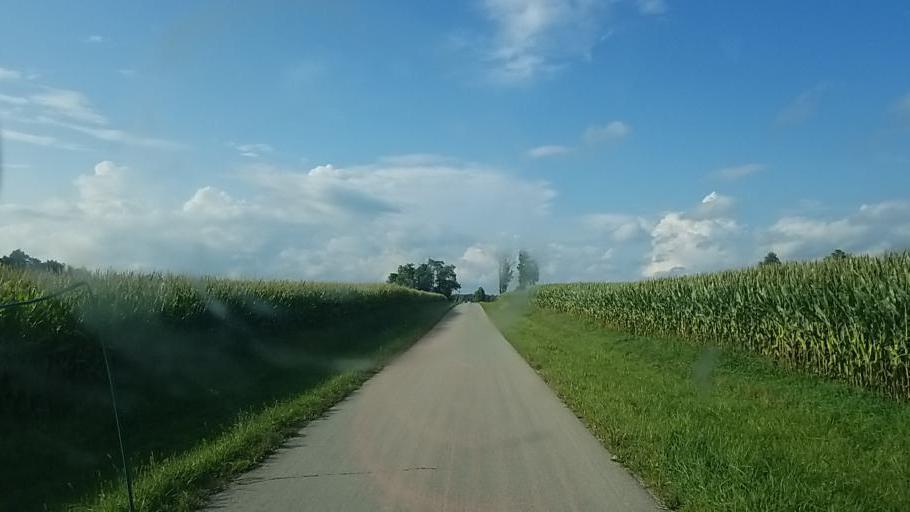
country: US
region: Ohio
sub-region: Wyandot County
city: Upper Sandusky
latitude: 40.8316
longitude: -83.1601
